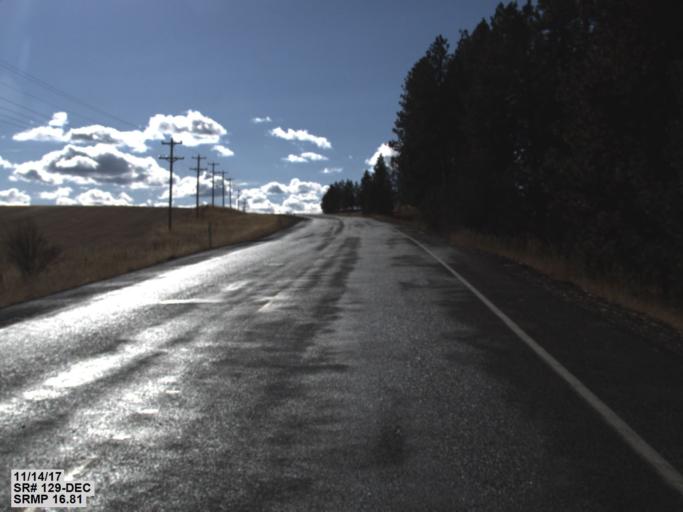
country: US
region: Washington
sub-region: Asotin County
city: Asotin
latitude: 46.1254
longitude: -117.1348
